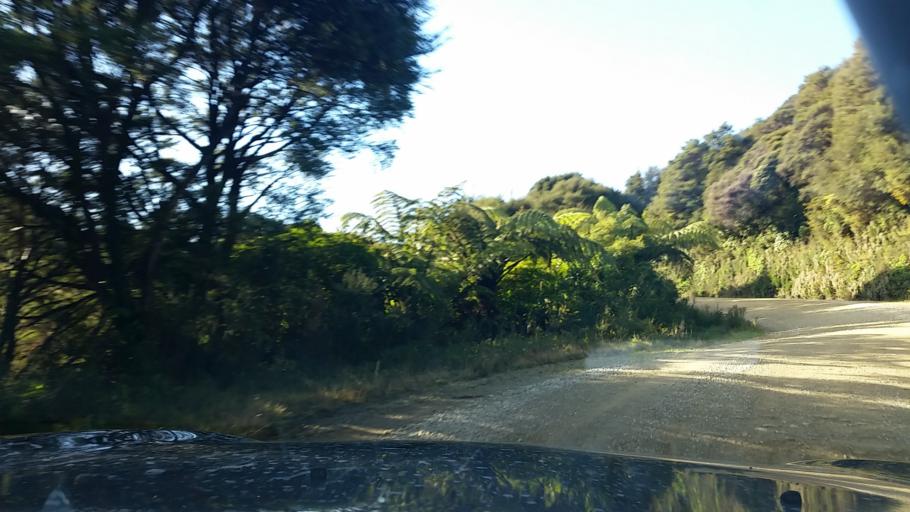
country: NZ
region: Marlborough
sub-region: Marlborough District
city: Picton
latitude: -41.1305
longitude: 174.1421
